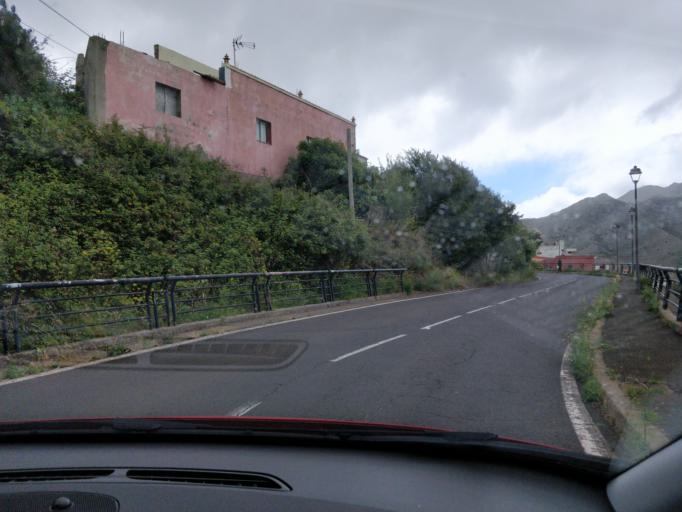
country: ES
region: Canary Islands
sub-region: Provincia de Santa Cruz de Tenerife
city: Tanque
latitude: 28.3269
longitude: -16.8438
